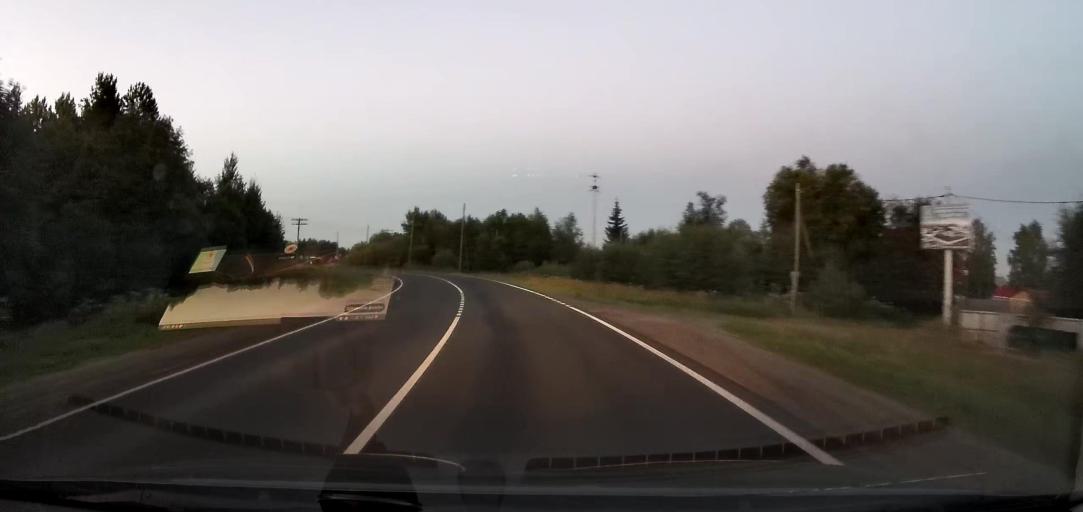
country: RU
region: Arkhangelskaya
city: Uyemskiy
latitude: 64.4154
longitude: 40.9906
